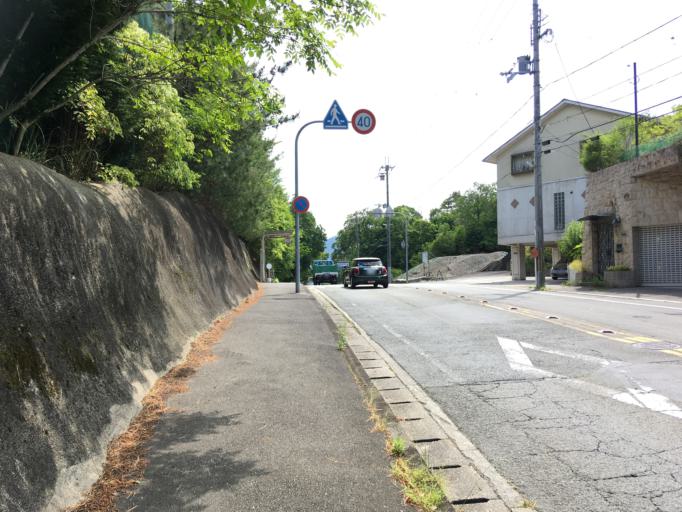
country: JP
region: Nara
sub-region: Ikoma-shi
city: Ikoma
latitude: 34.7111
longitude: 135.7128
